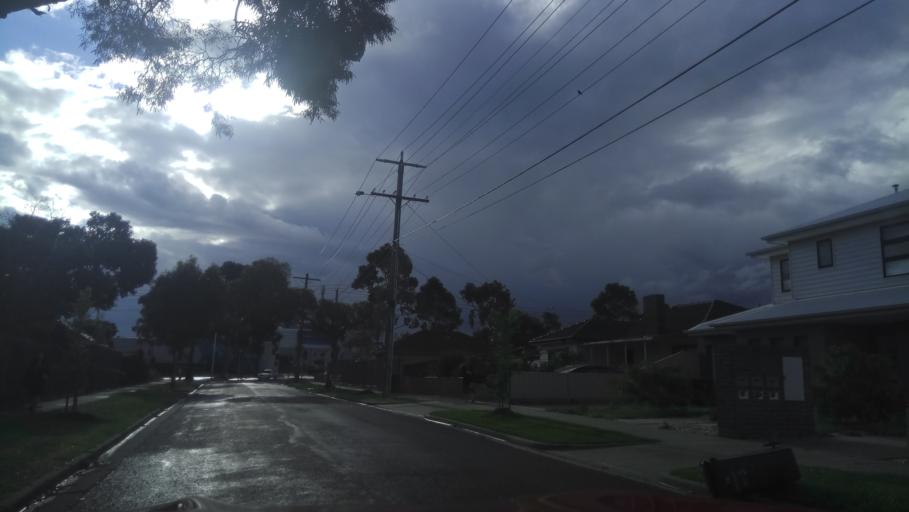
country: AU
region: Victoria
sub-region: Hobsons Bay
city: Altona North
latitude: -37.8281
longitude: 144.8499
